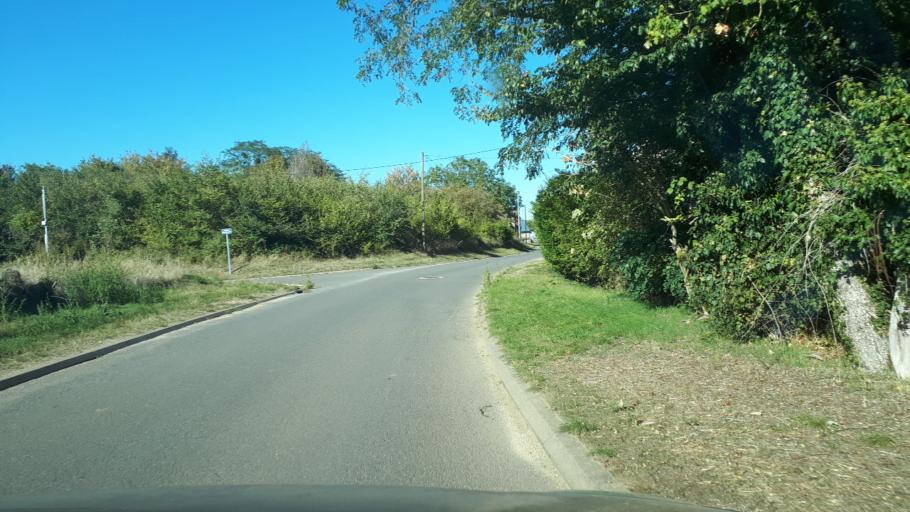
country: FR
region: Centre
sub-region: Departement du Cher
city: Baugy
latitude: 47.2070
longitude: 2.7409
